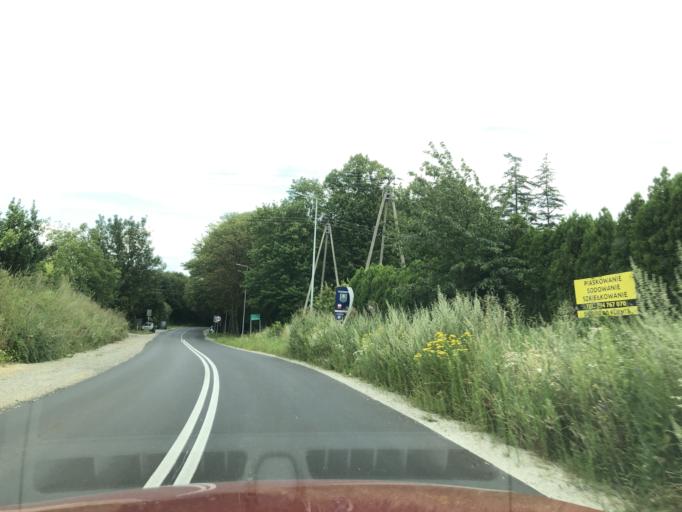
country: PL
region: Lower Silesian Voivodeship
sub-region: Powiat trzebnicki
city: Trzebnica
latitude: 51.3056
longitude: 17.0442
